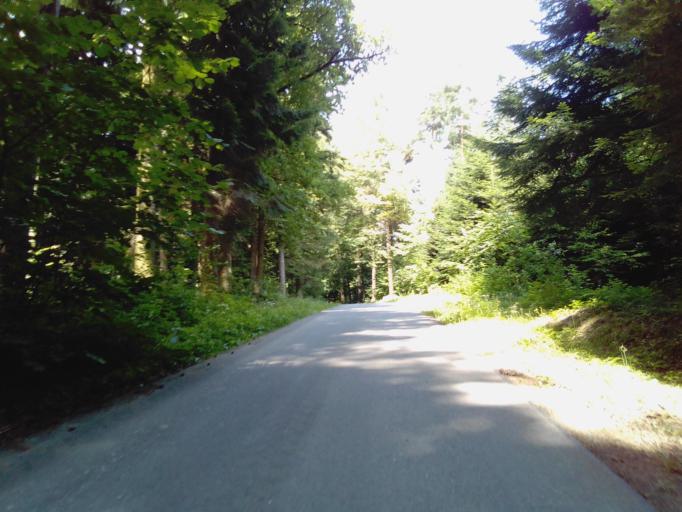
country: PL
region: Subcarpathian Voivodeship
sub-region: Powiat strzyzowski
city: Frysztak
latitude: 49.7899
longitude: 21.6027
